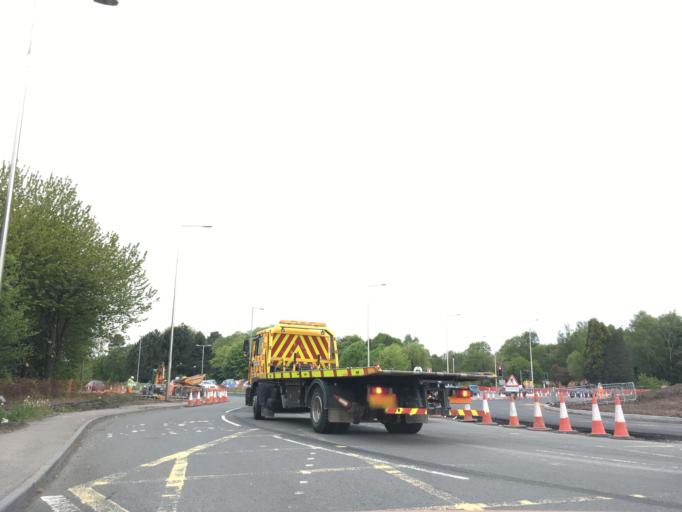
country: GB
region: Wales
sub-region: Newport
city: Newport
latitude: 51.5671
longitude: -3.0210
